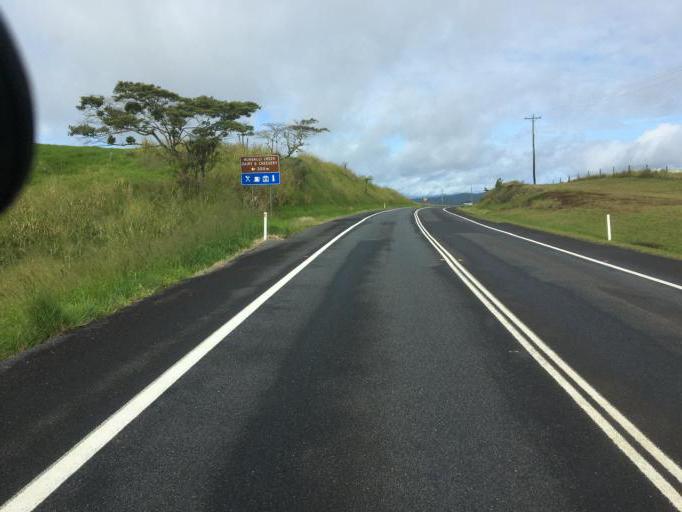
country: AU
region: Queensland
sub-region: Tablelands
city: Ravenshoe
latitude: -17.5366
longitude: 145.6644
